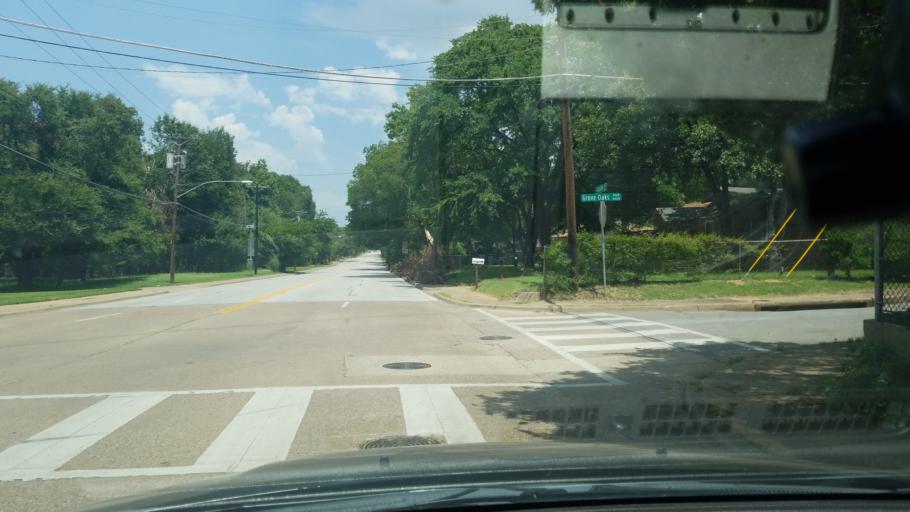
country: US
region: Texas
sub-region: Dallas County
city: Balch Springs
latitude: 32.7134
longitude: -96.6571
